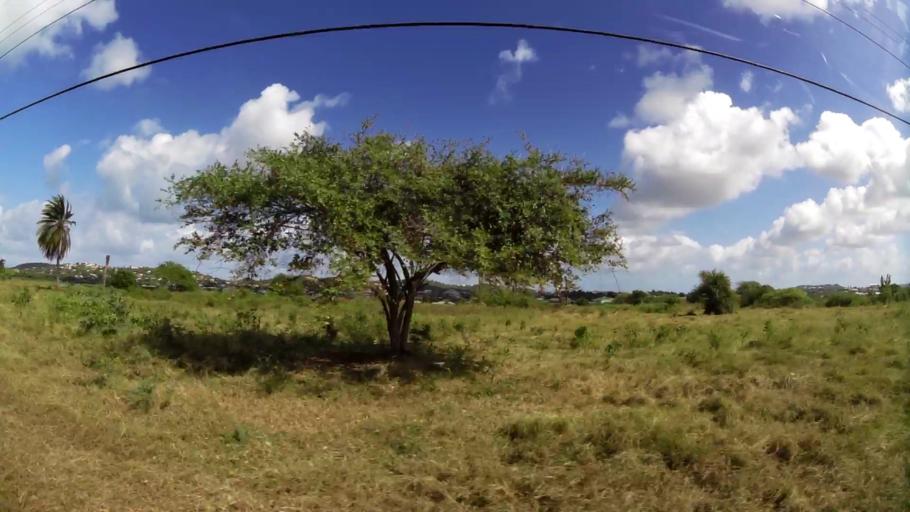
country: AG
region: Saint John
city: Saint John's
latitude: 17.1375
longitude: -61.8569
